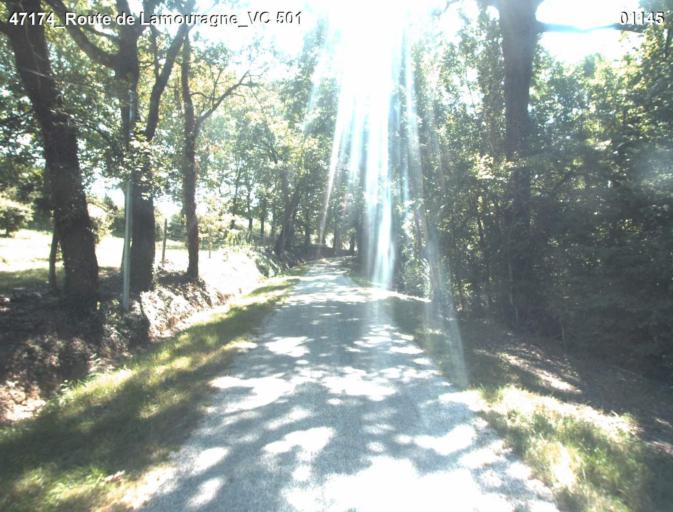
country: FR
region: Midi-Pyrenees
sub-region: Departement du Gers
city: Condom
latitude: 44.0379
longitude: 0.3889
